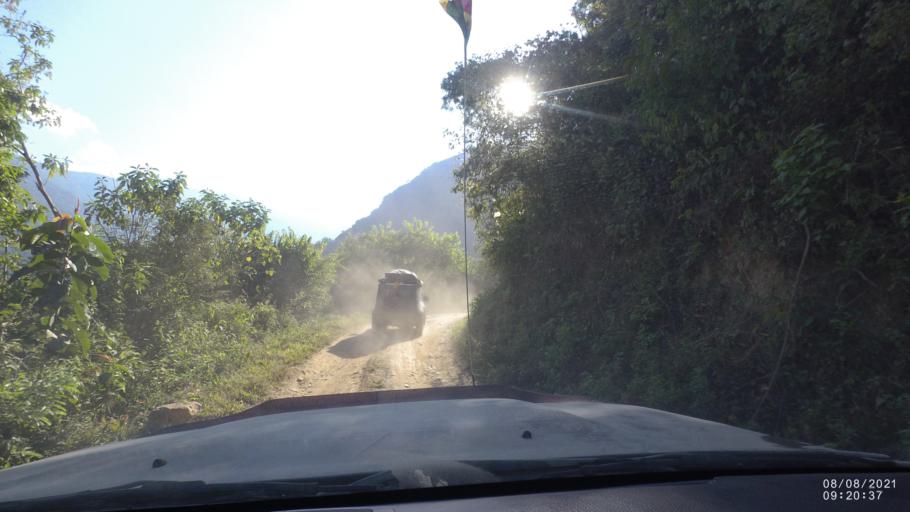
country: BO
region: La Paz
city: Quime
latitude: -16.5728
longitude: -66.7176
